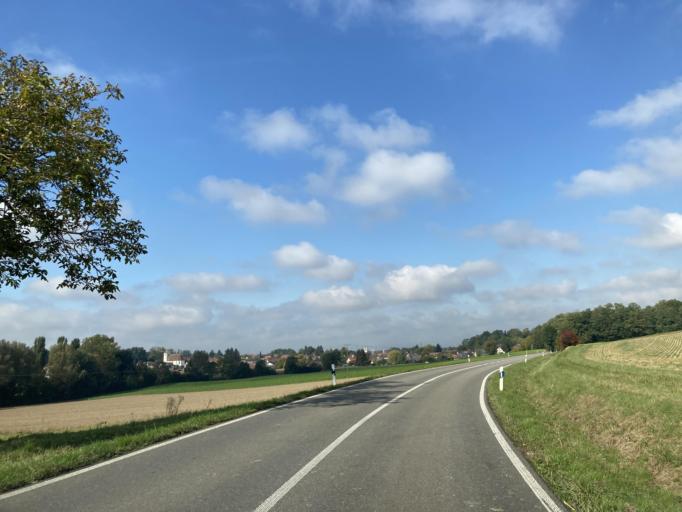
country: DE
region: Baden-Wuerttemberg
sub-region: Freiburg Region
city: Buggingen
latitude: 47.8399
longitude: 7.6481
